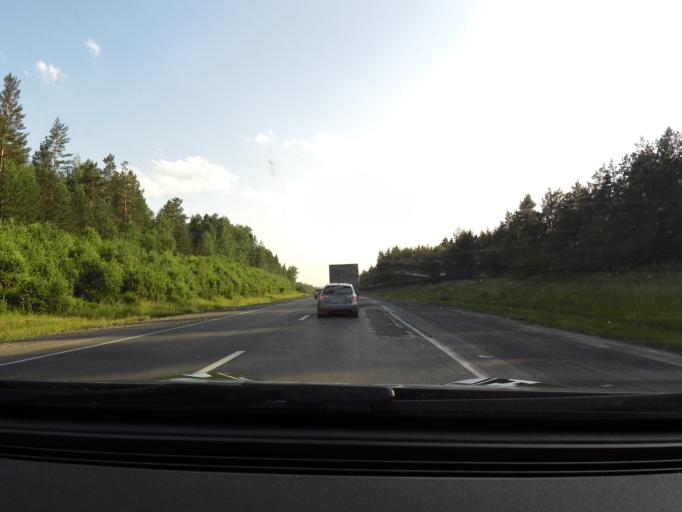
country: RU
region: Sverdlovsk
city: Druzhinino
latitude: 56.8181
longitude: 59.5645
